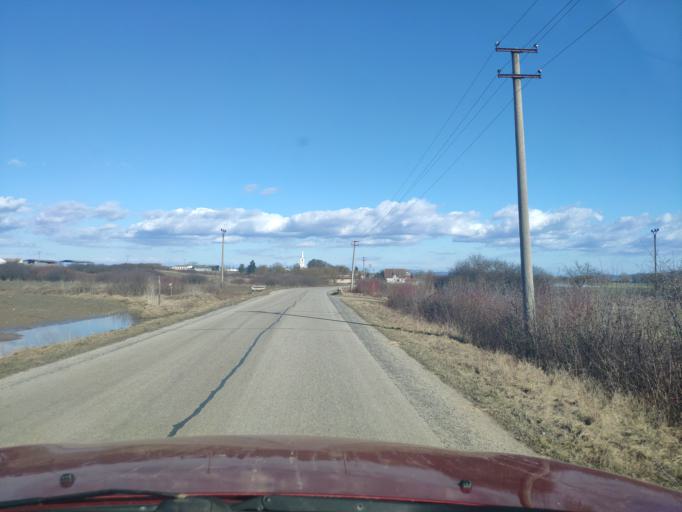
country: SK
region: Banskobystricky
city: Rimavska Sobota
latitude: 48.2902
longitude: 20.1437
